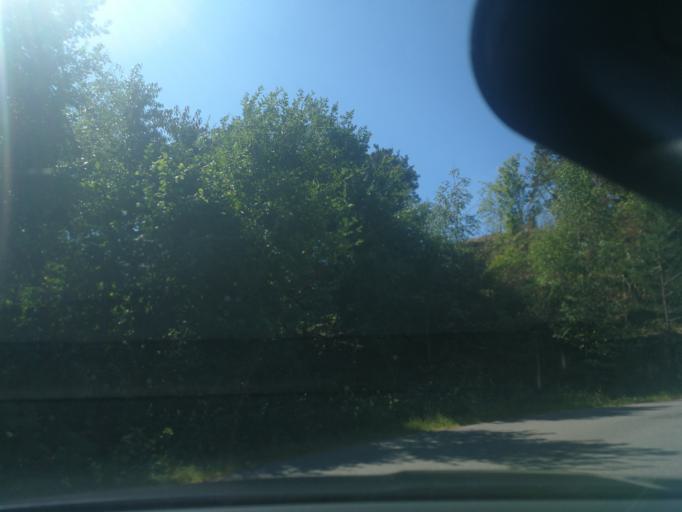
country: NO
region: Vestfold
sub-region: Stokke
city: Melsomvik
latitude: 59.2301
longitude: 10.3364
